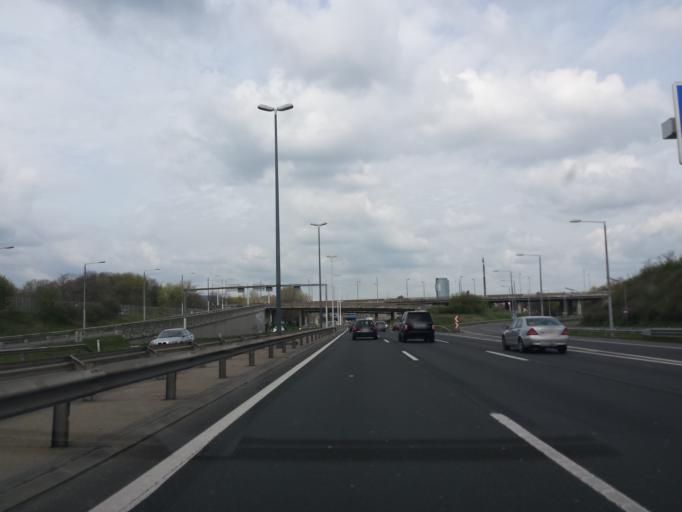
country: AT
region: Vienna
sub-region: Wien Stadt
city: Vienna
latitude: 48.2381
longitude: 16.4046
